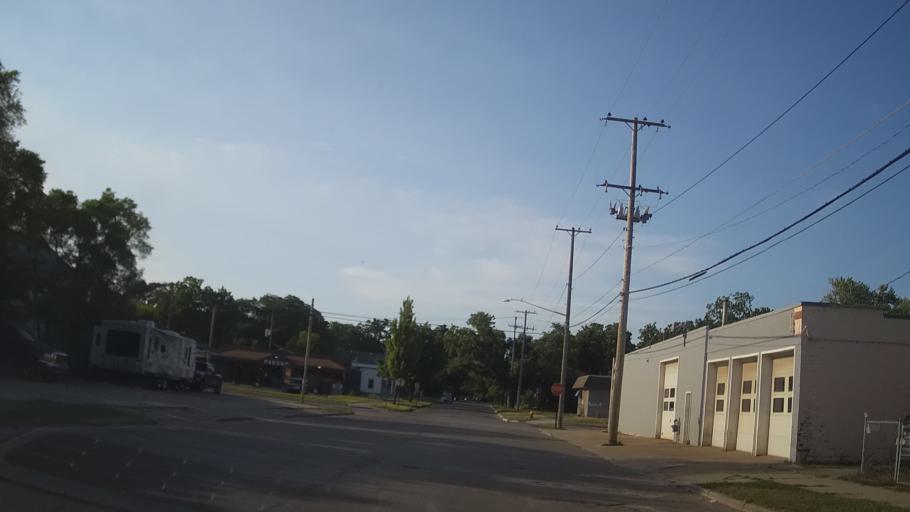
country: US
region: Michigan
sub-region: Grand Traverse County
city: Traverse City
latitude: 44.7589
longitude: -85.6112
